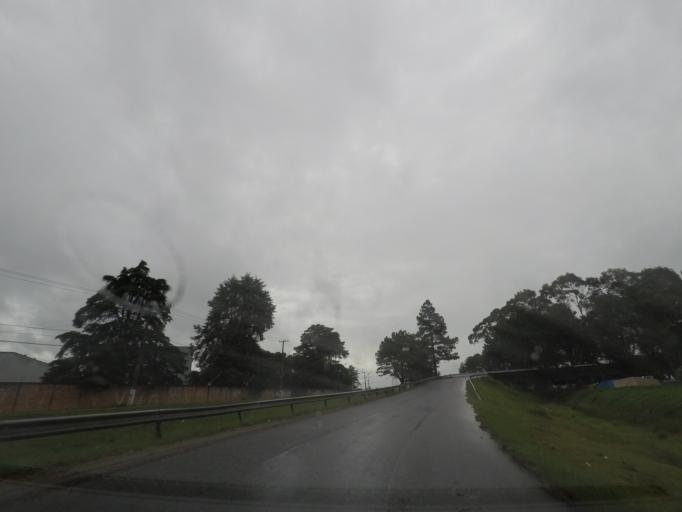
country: BR
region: Parana
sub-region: Curitiba
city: Curitiba
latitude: -25.4326
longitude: -49.3642
